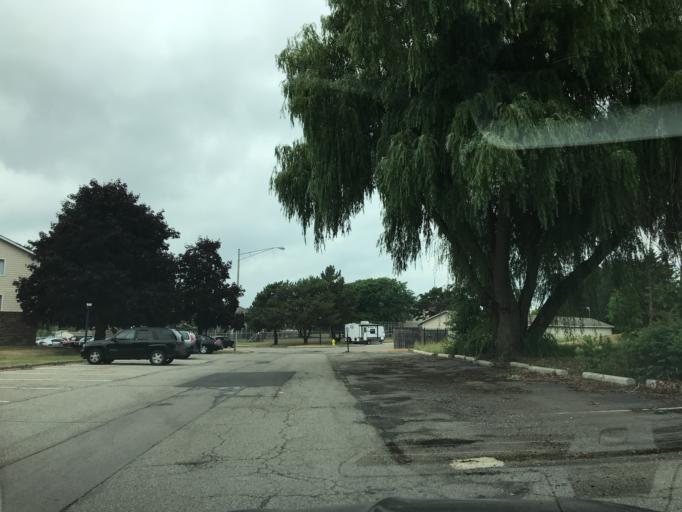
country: US
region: Michigan
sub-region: Eaton County
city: Waverly
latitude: 42.7378
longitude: -84.6626
